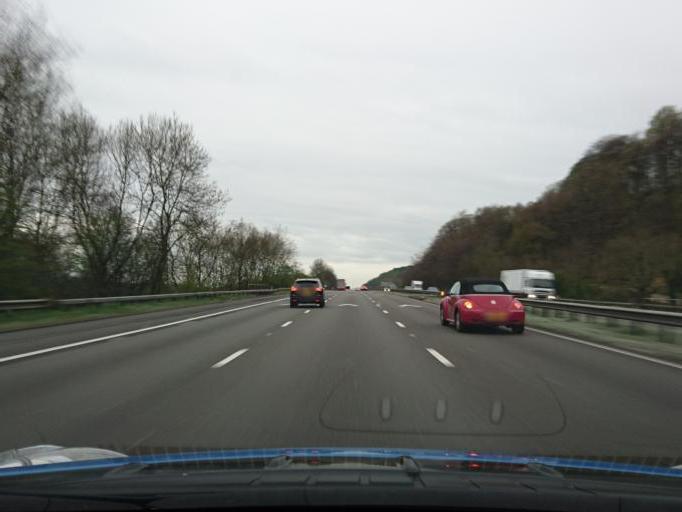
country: GB
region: England
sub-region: Staffordshire
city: Barlaston
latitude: 52.9474
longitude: -2.2173
